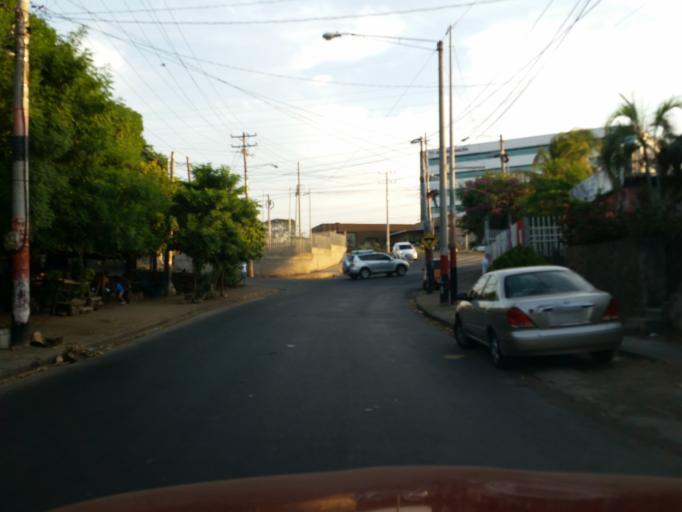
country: NI
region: Managua
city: Managua
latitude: 12.1098
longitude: -86.2511
